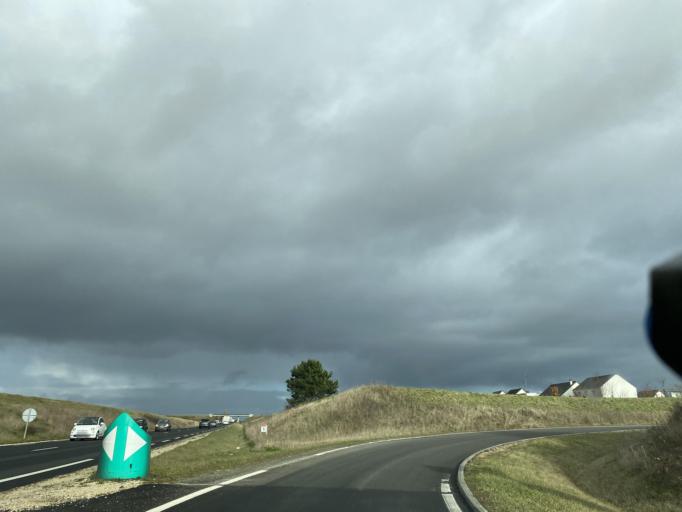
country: FR
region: Centre
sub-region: Departement d'Eure-et-Loir
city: Mainvilliers
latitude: 48.4578
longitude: 1.4518
